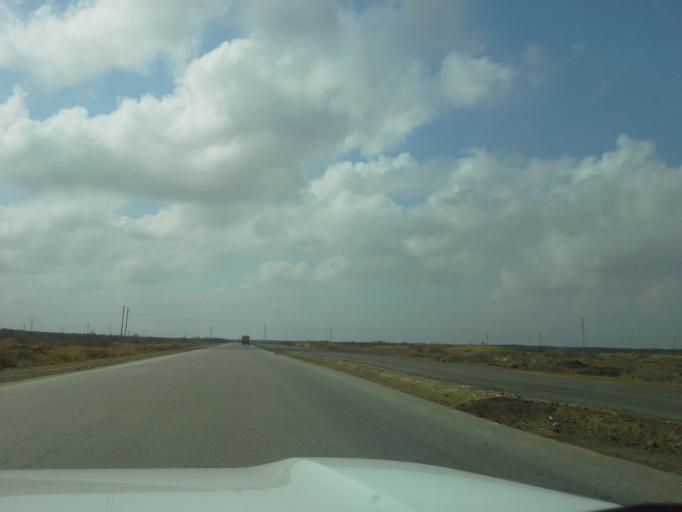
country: TM
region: Mary
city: Mary
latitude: 37.3358
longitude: 61.4226
